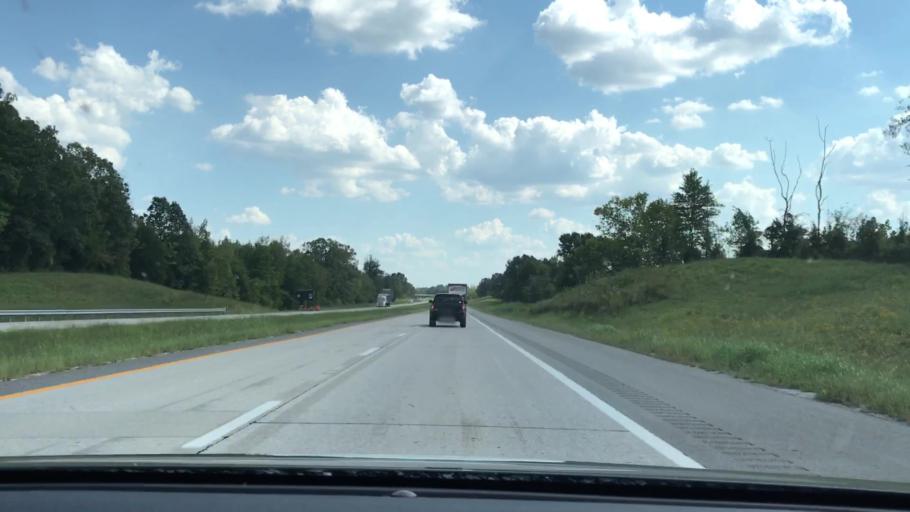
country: US
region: Kentucky
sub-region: Ohio County
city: Oak Grove
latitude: 37.3613
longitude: -86.7940
